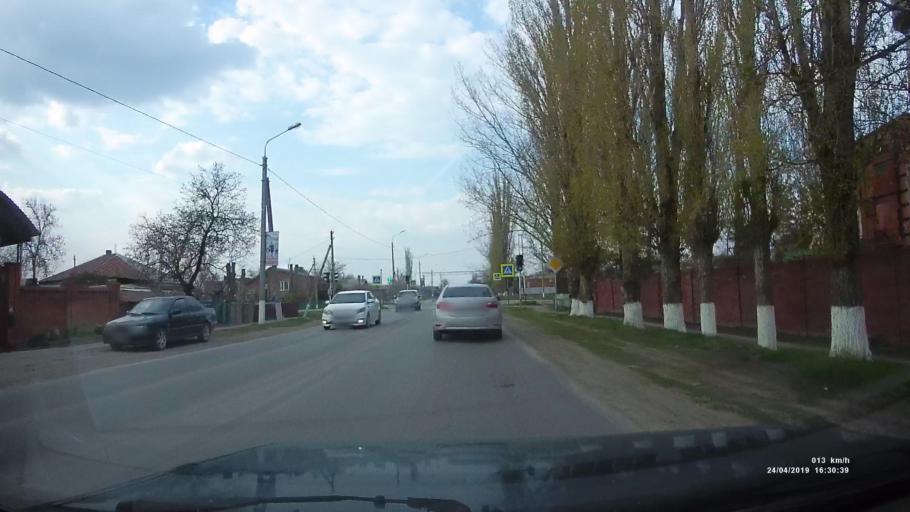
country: RU
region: Rostov
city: Orlovskiy
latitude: 46.8756
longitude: 42.0384
